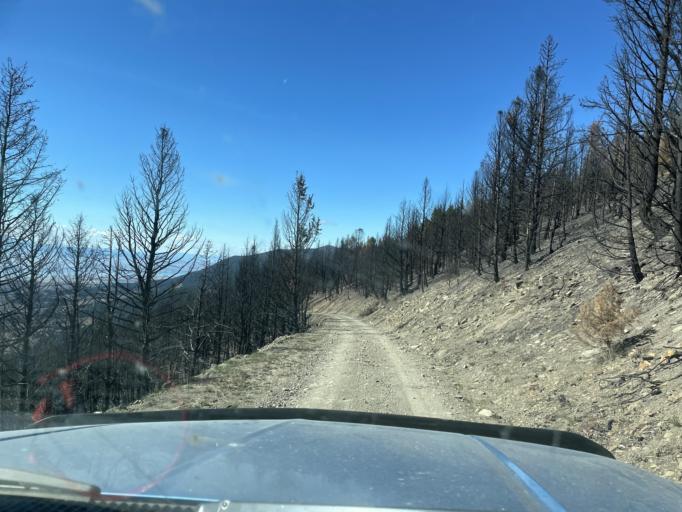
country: US
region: Montana
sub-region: Broadwater County
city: Townsend
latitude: 46.5011
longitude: -111.2722
